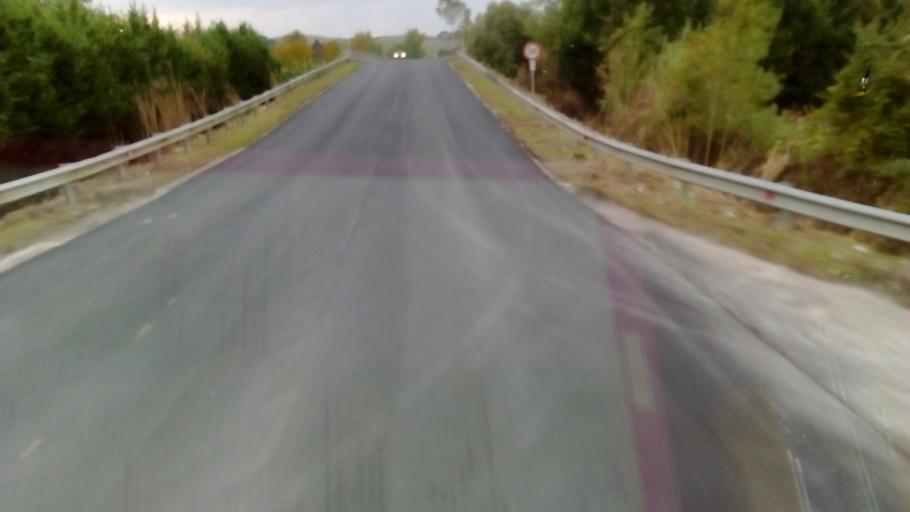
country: IT
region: Tuscany
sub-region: Province of Florence
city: Castelfiorentino
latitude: 43.5929
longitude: 10.9792
